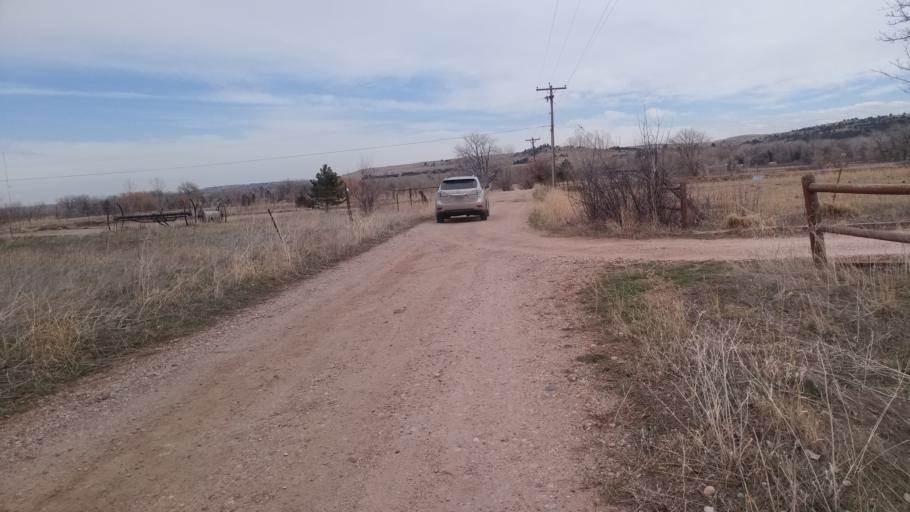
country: US
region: Colorado
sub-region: Boulder County
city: Boulder
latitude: 39.9605
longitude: -105.2421
